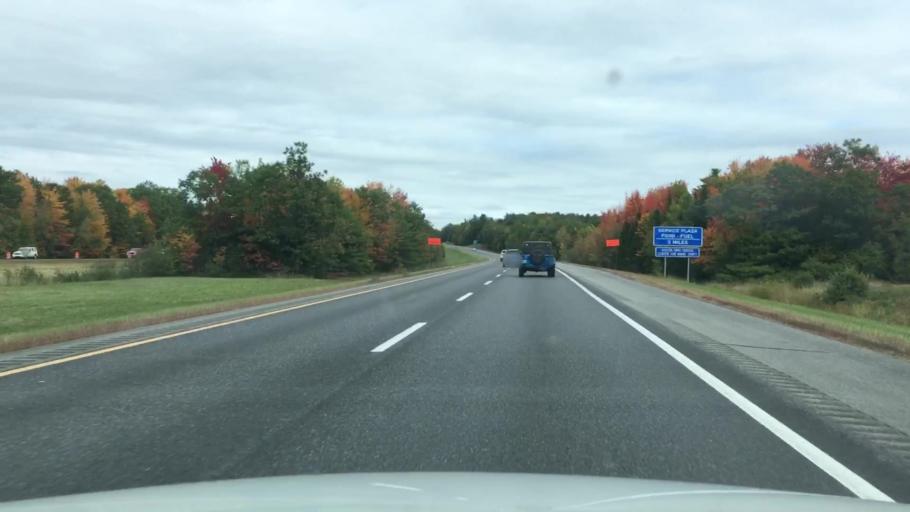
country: US
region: Maine
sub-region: Sagadahoc County
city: Richmond
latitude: 44.1564
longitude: -69.8362
